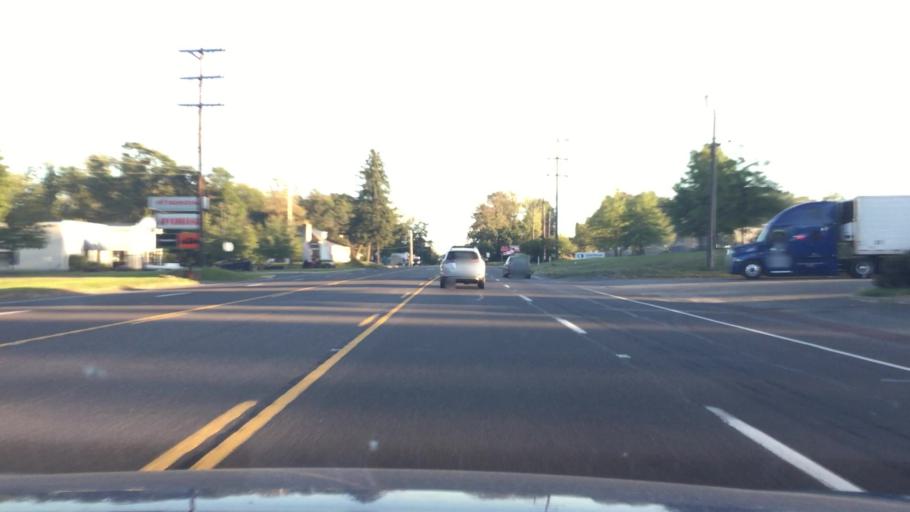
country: US
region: Pennsylvania
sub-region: Lehigh County
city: Coopersburg
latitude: 40.4928
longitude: -75.3808
